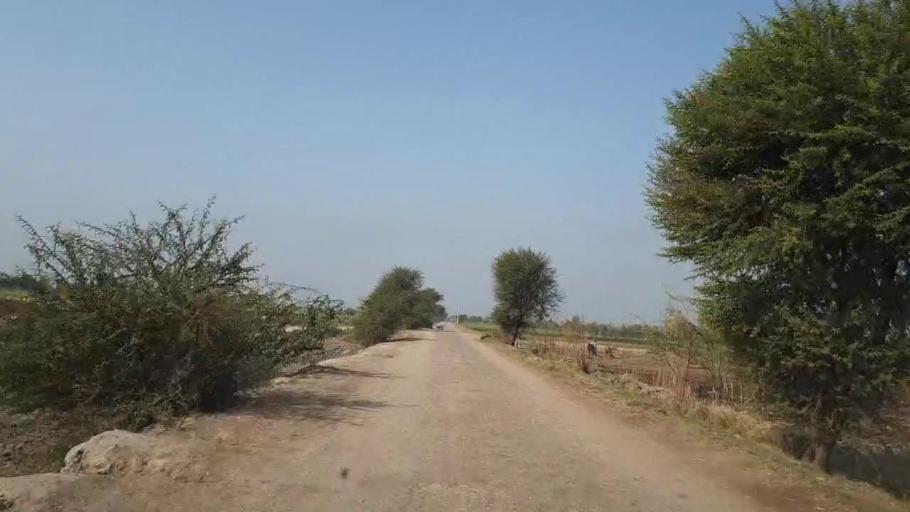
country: PK
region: Sindh
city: Mirpur Khas
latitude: 25.5821
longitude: 69.0159
